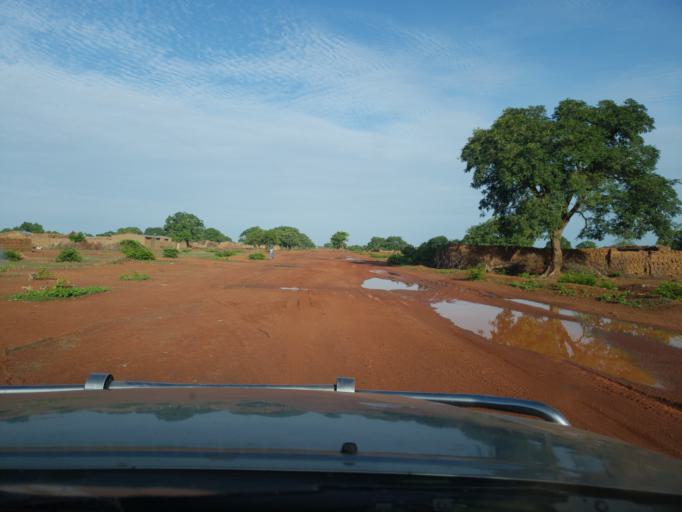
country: ML
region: Sikasso
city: Koutiala
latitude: 12.4293
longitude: -5.6164
